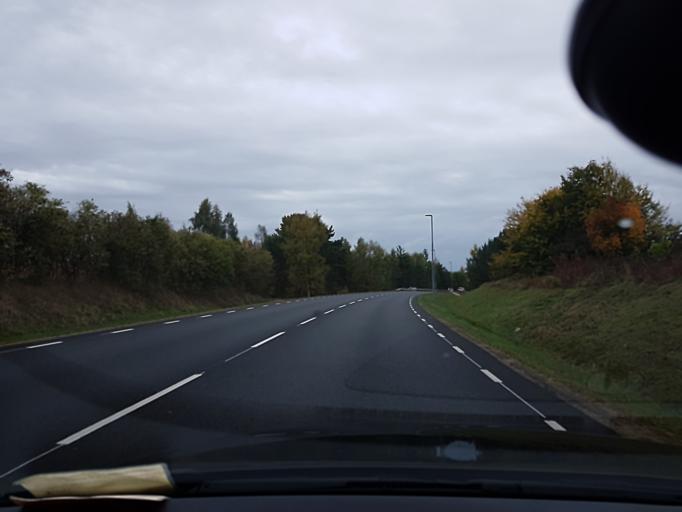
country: SE
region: Kronoberg
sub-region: Vaxjo Kommun
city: Vaexjoe
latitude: 56.9112
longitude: 14.7997
